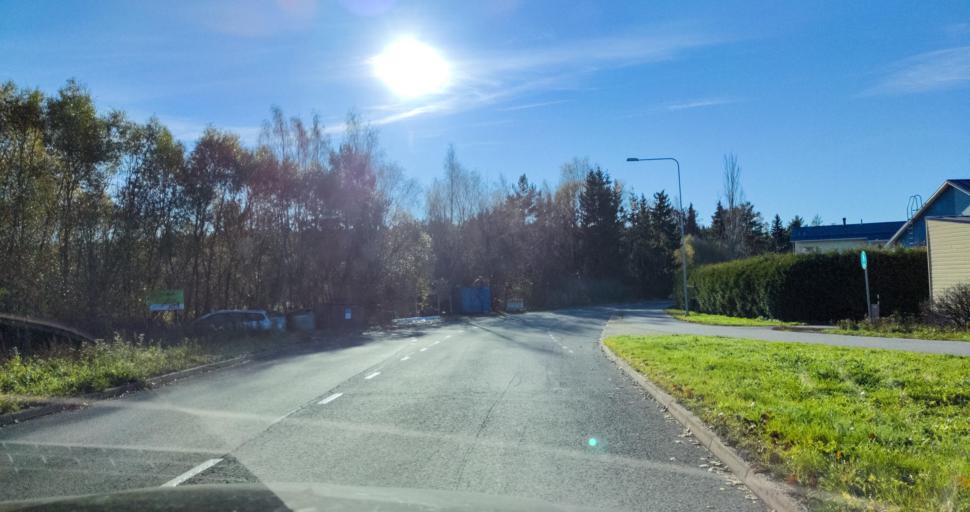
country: FI
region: Varsinais-Suomi
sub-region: Turku
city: Turku
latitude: 60.4088
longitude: 22.2208
